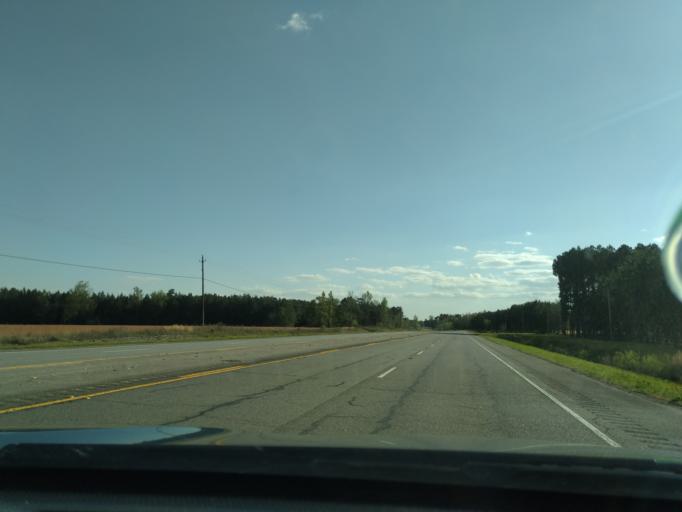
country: US
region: South Carolina
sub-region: Williamsburg County
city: Kingstree
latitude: 33.6288
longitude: -79.9227
